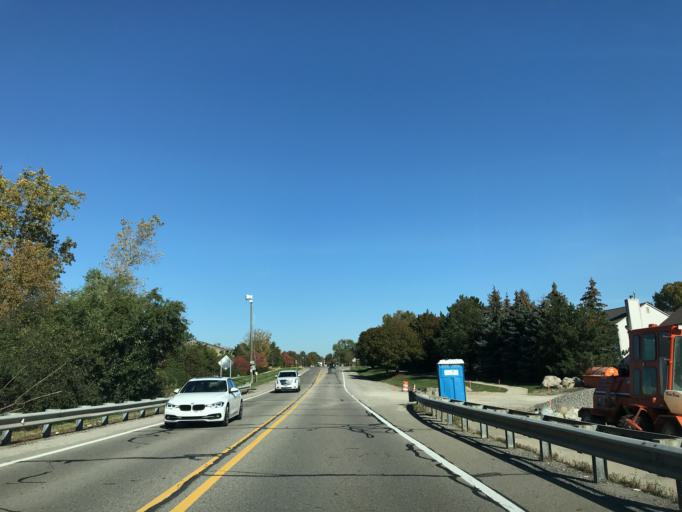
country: US
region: Michigan
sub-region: Oakland County
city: Farmington Hills
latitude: 42.4939
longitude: -83.3389
